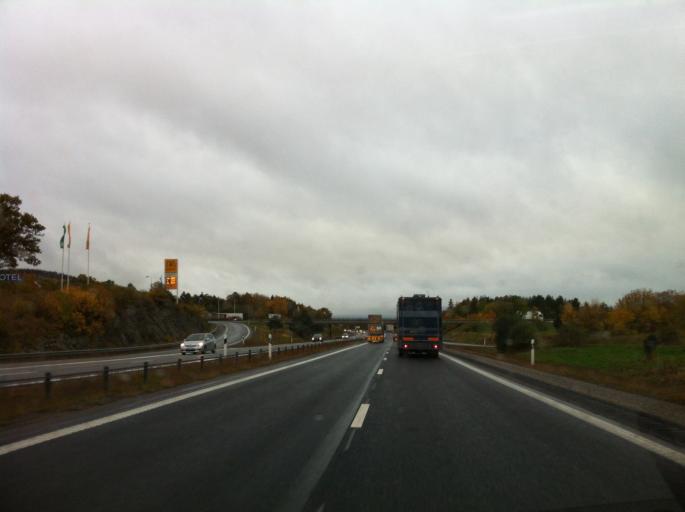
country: SE
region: Joenkoeping
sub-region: Jonkopings Kommun
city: Kaxholmen
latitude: 57.9264
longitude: 14.3203
